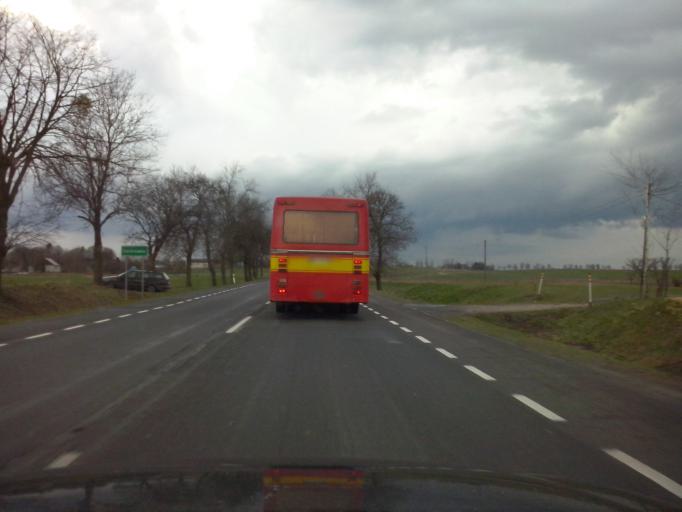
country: PL
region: Lublin Voivodeship
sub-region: Powiat chelmski
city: Rejowiec Fabryczny
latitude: 51.1731
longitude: 23.2818
